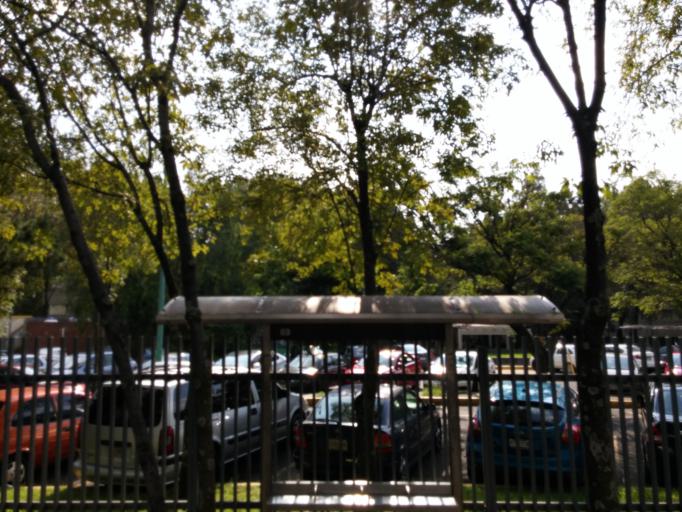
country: MX
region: Mexico City
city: Coyoacan
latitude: 19.3265
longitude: -99.1751
